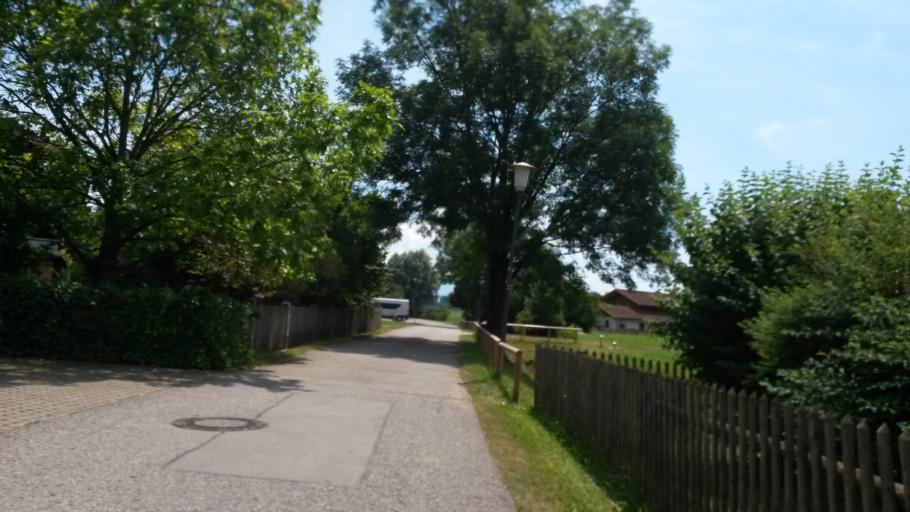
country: DE
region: Bavaria
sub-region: Upper Bavaria
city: Seeon-Seebruck
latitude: 47.9563
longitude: 12.5001
